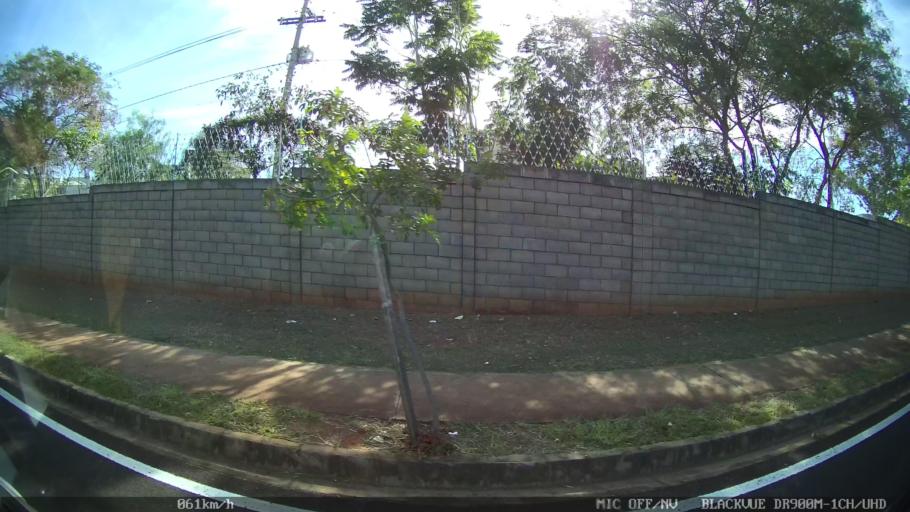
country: BR
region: Sao Paulo
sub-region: Sao Jose Do Rio Preto
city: Sao Jose do Rio Preto
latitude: -20.8082
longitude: -49.3337
